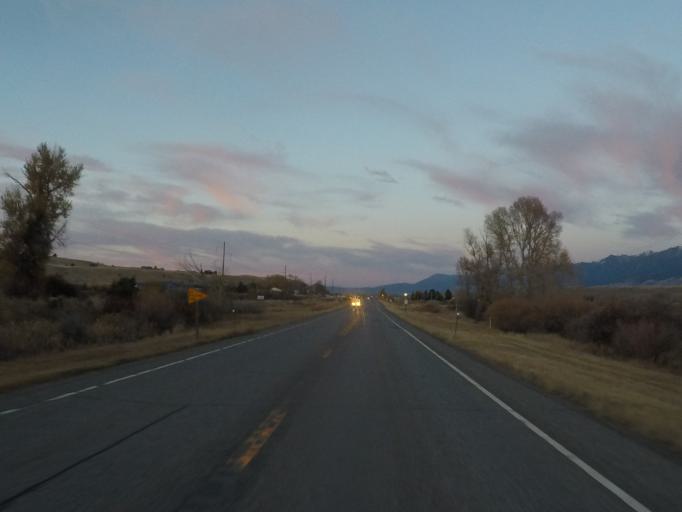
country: US
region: Montana
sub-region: Park County
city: Livingston
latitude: 45.3646
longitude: -110.7377
